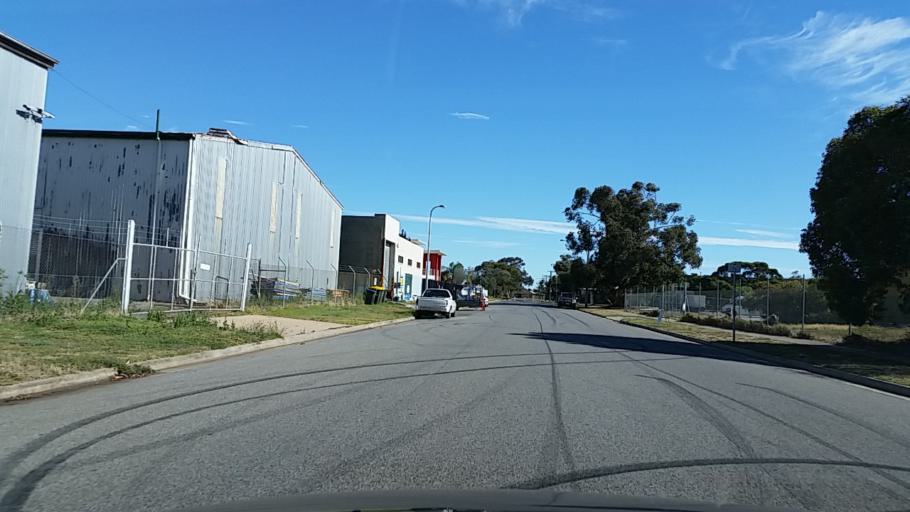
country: AU
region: South Australia
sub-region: Port Adelaide Enfield
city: Cheltenham
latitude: -34.8643
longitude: 138.5072
